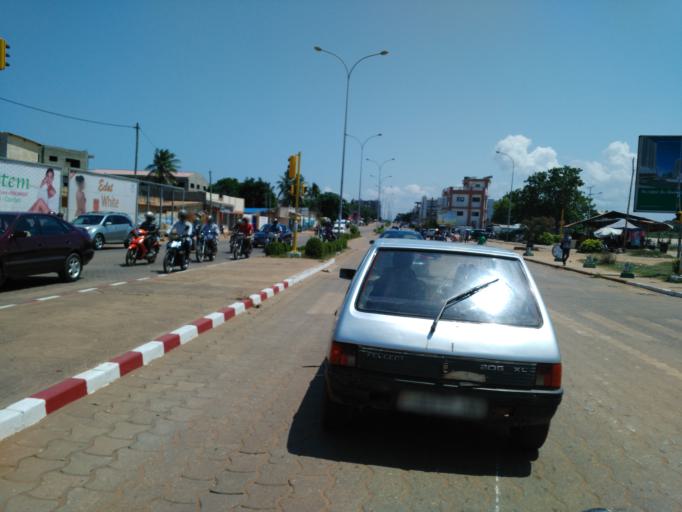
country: TG
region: Maritime
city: Lome
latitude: 6.1651
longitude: 1.2225
